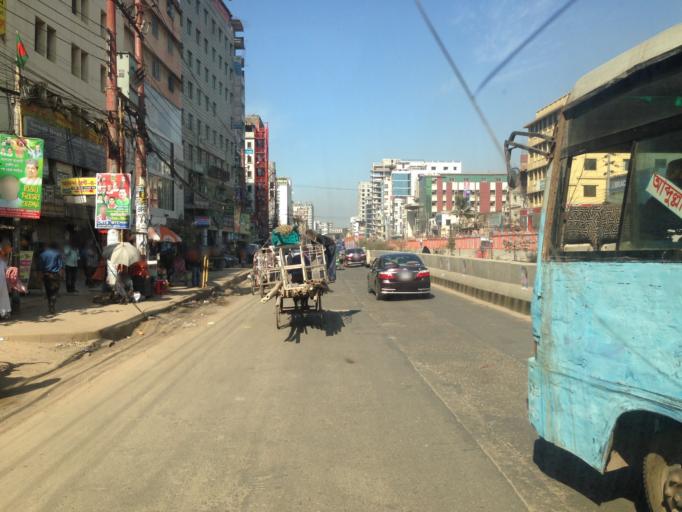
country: BD
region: Dhaka
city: Tungi
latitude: 23.8160
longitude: 90.3661
